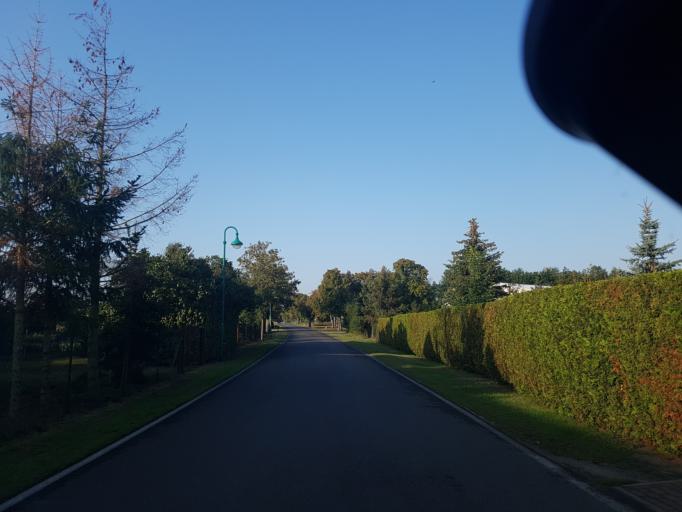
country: DE
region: Saxony-Anhalt
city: Holzdorf
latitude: 51.8133
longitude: 13.1455
